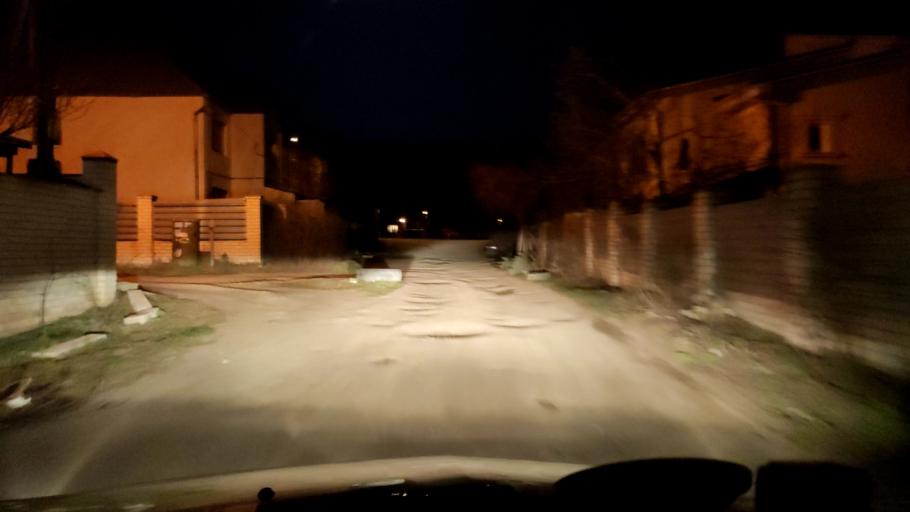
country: RU
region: Voronezj
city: Pridonskoy
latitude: 51.6175
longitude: 39.0581
